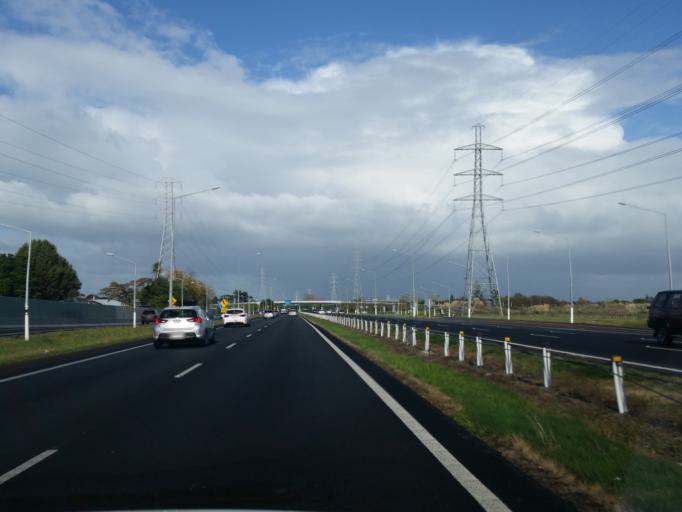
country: NZ
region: Auckland
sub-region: Auckland
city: Papakura
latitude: -37.0689
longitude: 174.9272
